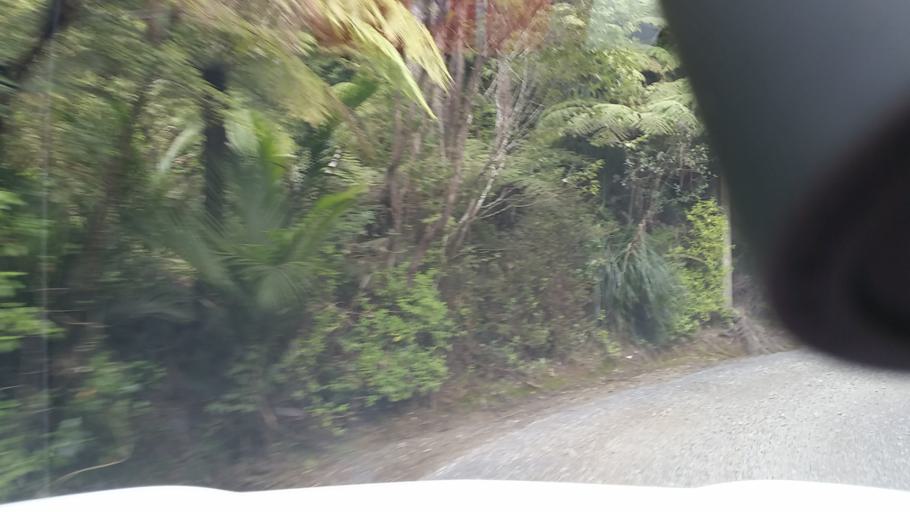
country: NZ
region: Auckland
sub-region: Auckland
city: Muriwai Beach
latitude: -36.8729
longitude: 174.5088
